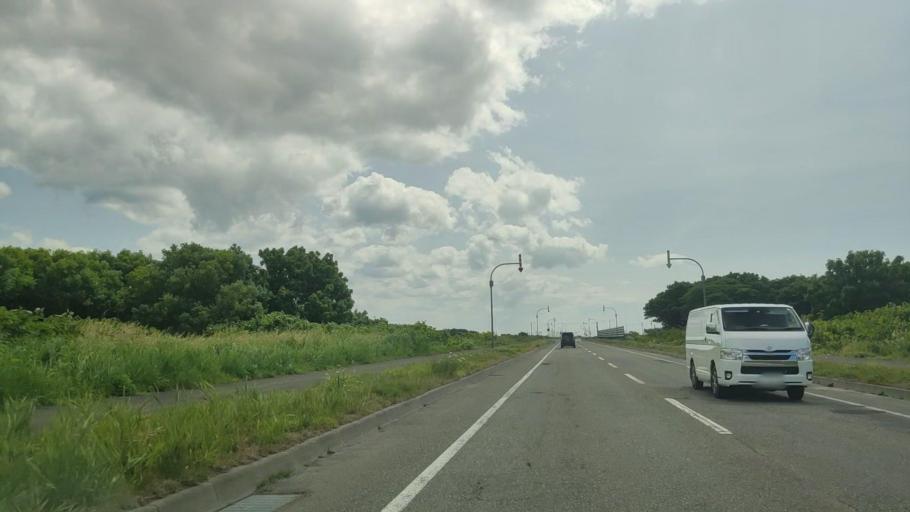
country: JP
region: Hokkaido
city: Makubetsu
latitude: 44.8755
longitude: 141.7510
